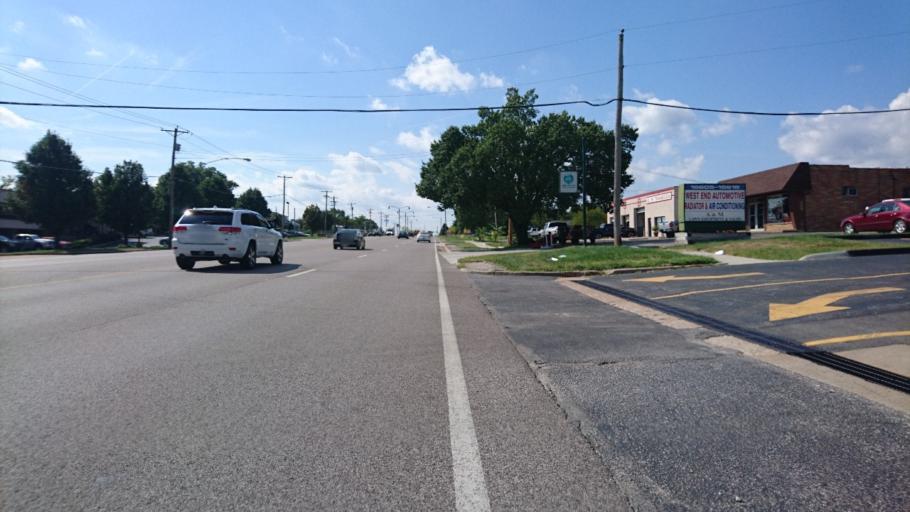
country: US
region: Missouri
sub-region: Saint Louis County
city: Ellisville
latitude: 38.5928
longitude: -90.5724
